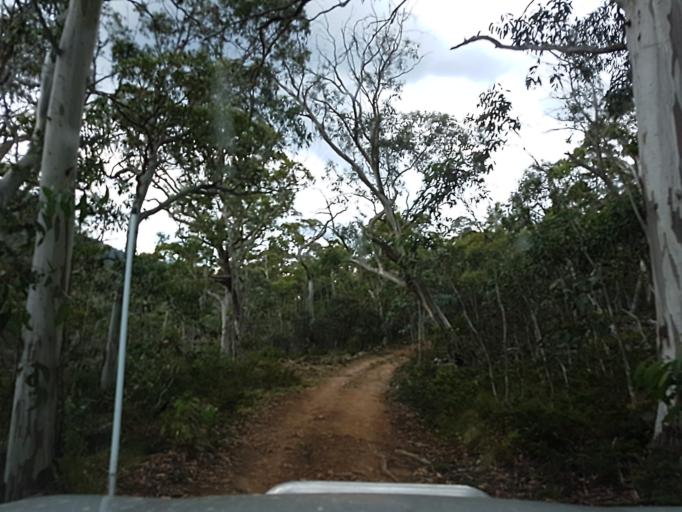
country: AU
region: New South Wales
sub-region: Snowy River
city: Jindabyne
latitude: -36.8834
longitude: 148.1558
